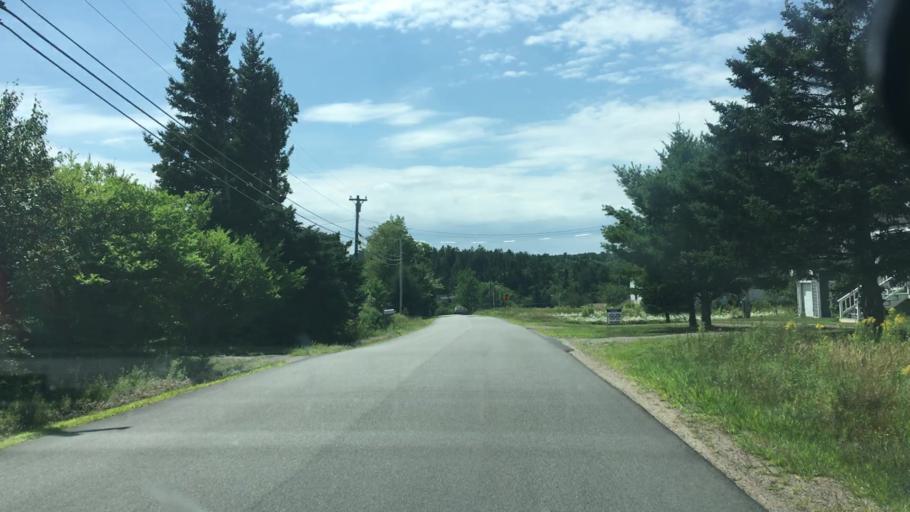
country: CA
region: New Brunswick
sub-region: Charlotte County
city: Saint Andrews
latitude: 44.9762
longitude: -67.0714
